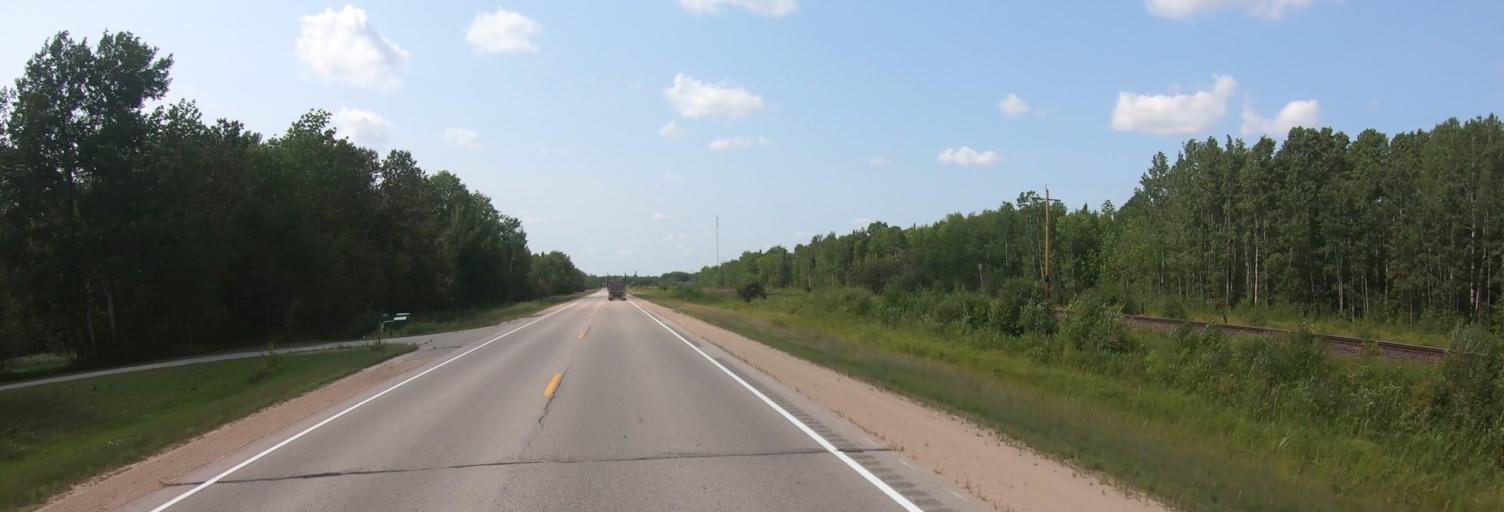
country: US
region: Minnesota
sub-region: Roseau County
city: Warroad
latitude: 48.7948
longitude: -95.0733
